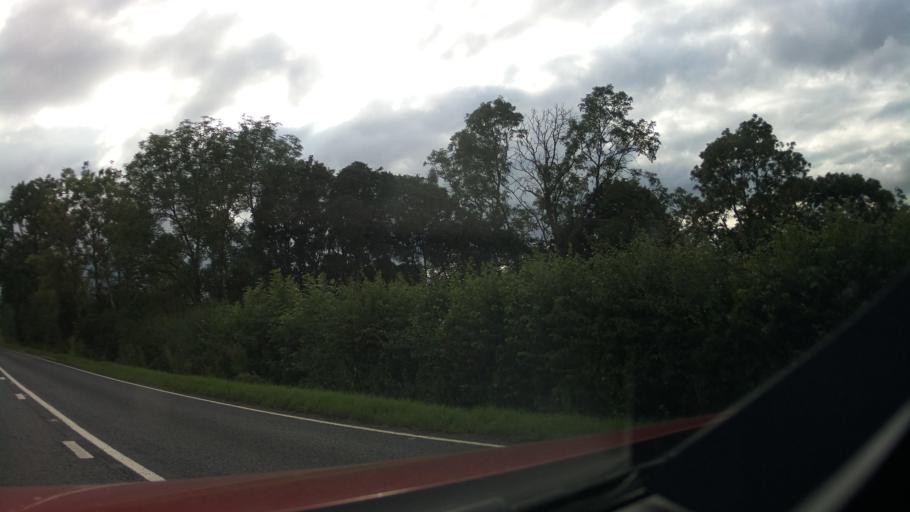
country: GB
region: England
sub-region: Warwickshire
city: Dunchurch
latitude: 52.3030
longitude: -1.3160
